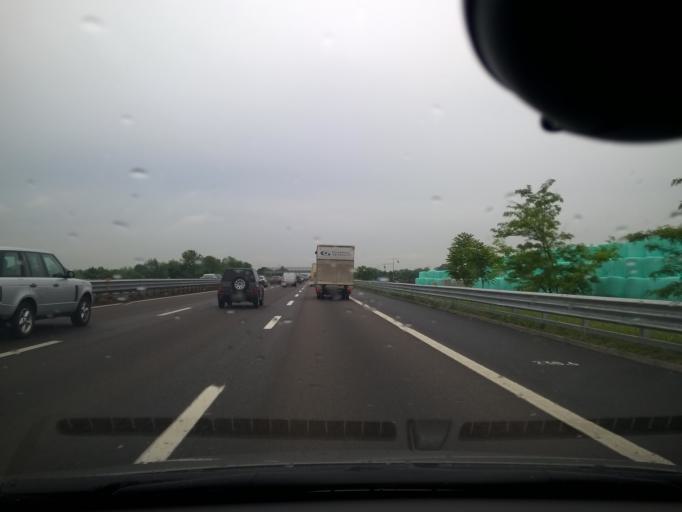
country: IT
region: Lombardy
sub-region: Provincia di Brescia
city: Molinetto
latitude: 45.4761
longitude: 10.3487
